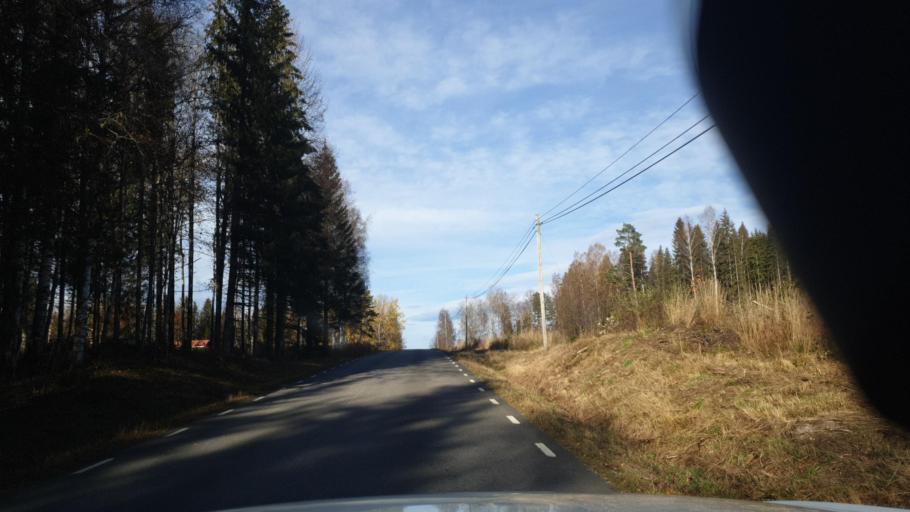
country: SE
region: Vaermland
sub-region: Eda Kommun
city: Amotfors
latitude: 59.9220
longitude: 12.5202
